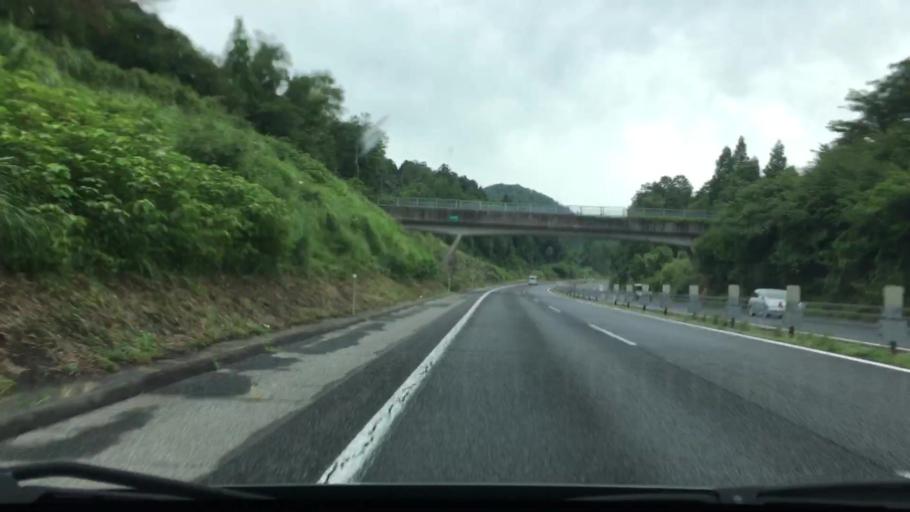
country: JP
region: Hiroshima
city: Hiroshima-shi
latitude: 34.6272
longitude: 132.5105
